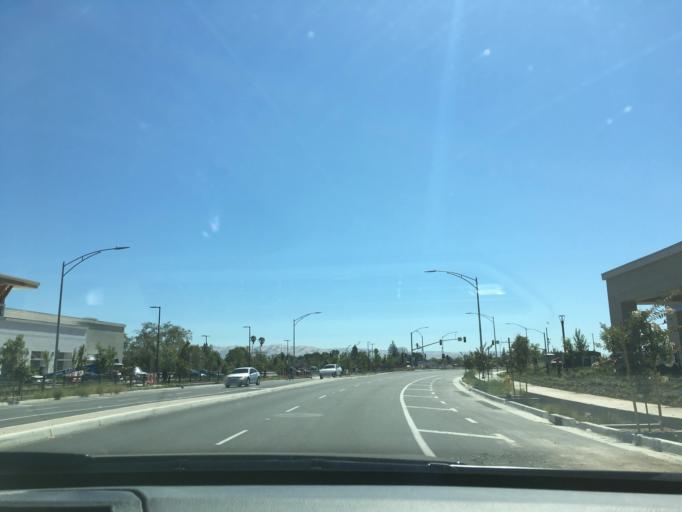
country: US
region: California
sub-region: Santa Clara County
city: Seven Trees
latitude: 37.2592
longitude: -121.8738
